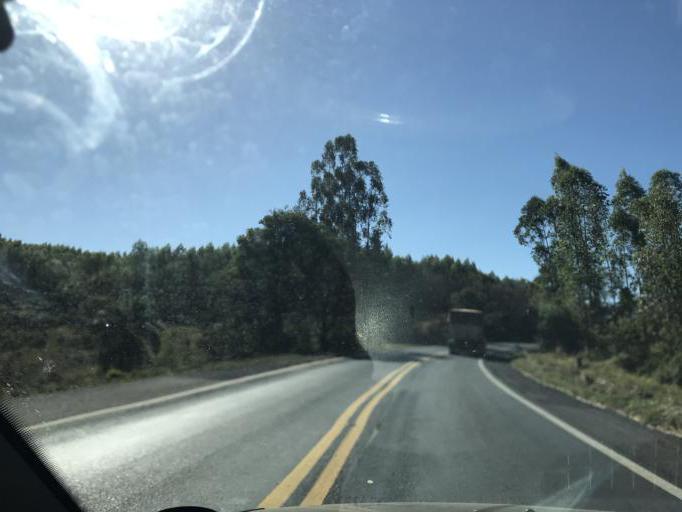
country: BR
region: Minas Gerais
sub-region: Bambui
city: Bambui
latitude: -19.8707
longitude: -45.9864
